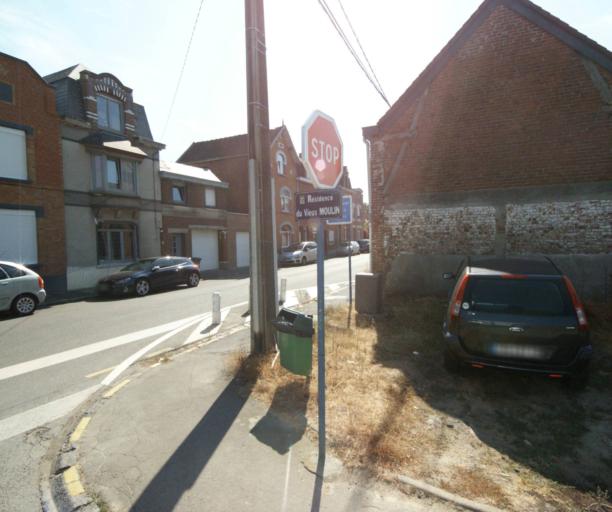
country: FR
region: Nord-Pas-de-Calais
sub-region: Departement du Nord
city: Halluin
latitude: 50.7798
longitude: 3.1347
